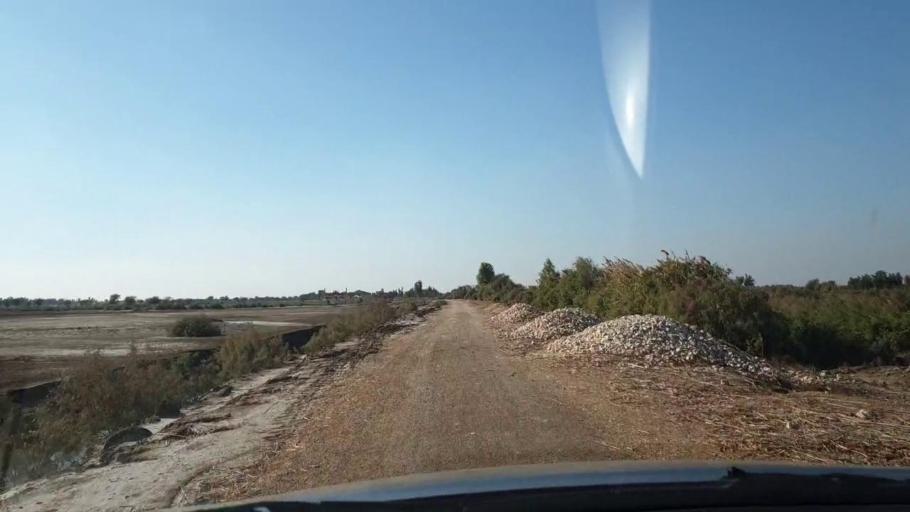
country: PK
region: Sindh
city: Jhol
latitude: 25.8922
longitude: 69.0257
